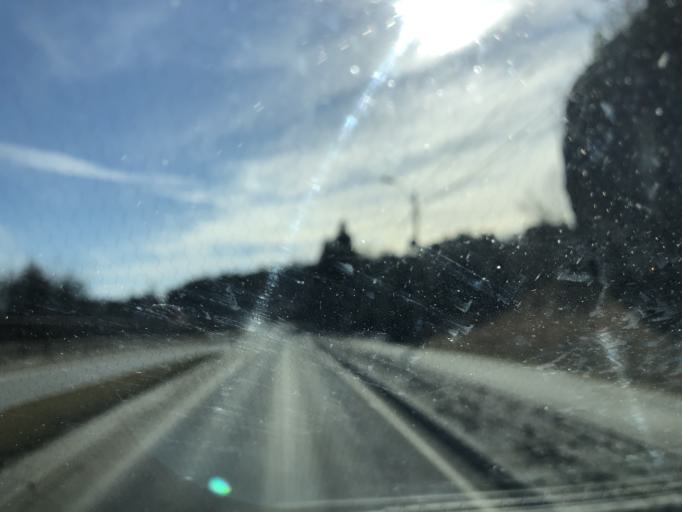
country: NO
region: Telemark
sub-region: Porsgrunn
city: Porsgrunn
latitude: 59.0977
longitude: 9.6852
